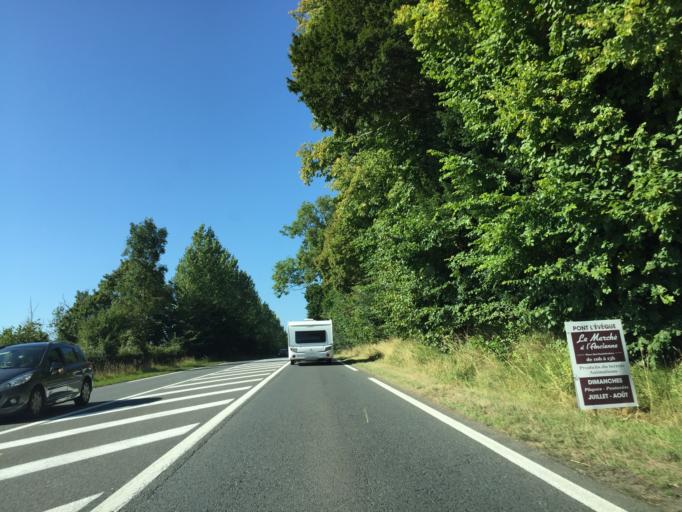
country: FR
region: Lower Normandy
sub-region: Departement du Calvados
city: Saint-Gatien-des-Bois
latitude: 49.2748
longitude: 0.2164
